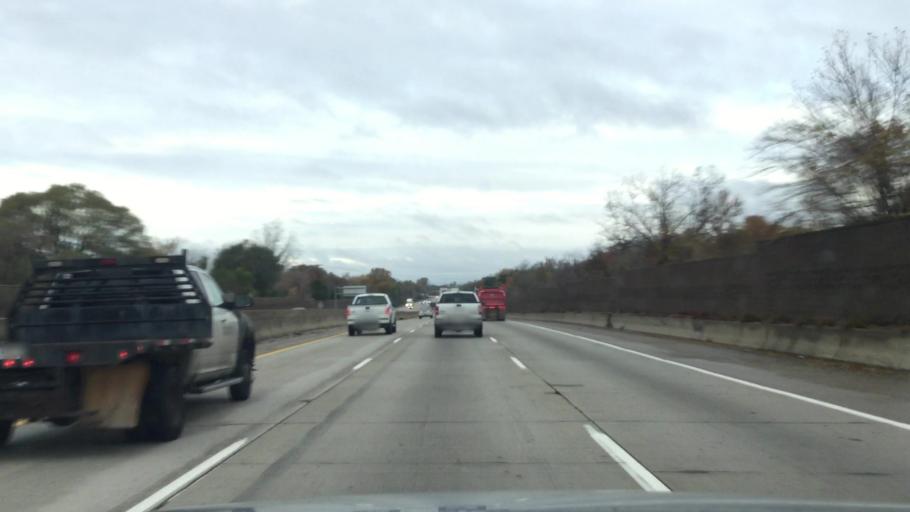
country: US
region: Michigan
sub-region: Washtenaw County
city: Ypsilanti
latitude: 42.2207
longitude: -83.5630
